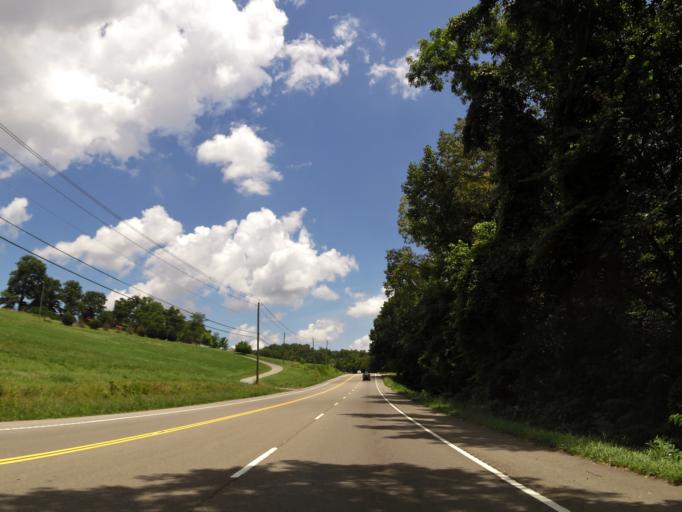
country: US
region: Tennessee
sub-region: Union County
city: Maynardville
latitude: 36.2704
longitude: -83.7702
